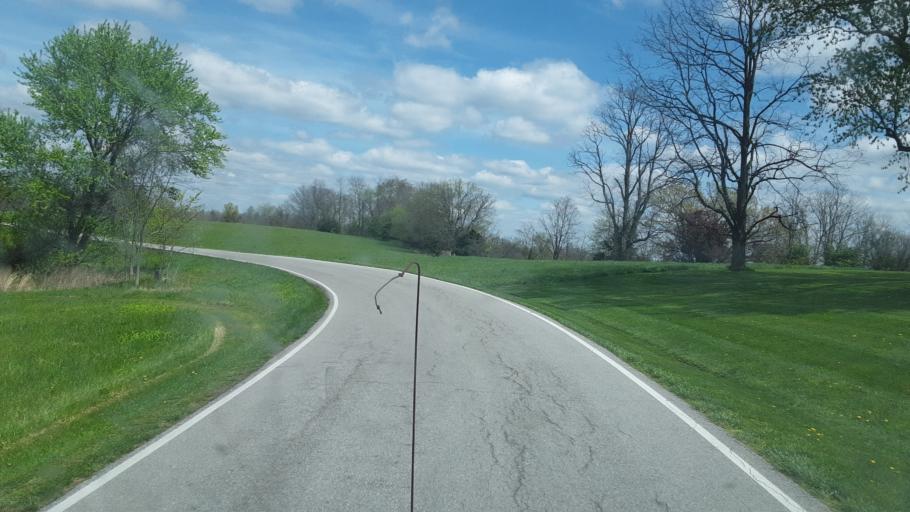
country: US
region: Kentucky
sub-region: Owen County
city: Owenton
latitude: 38.6535
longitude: -84.7716
